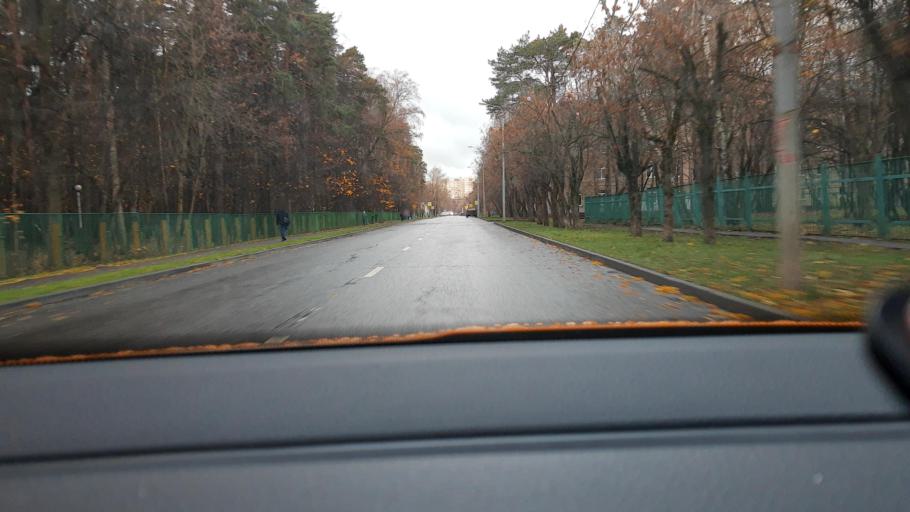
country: RU
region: Moscow
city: Yaroslavskiy
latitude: 55.8846
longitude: 37.7042
